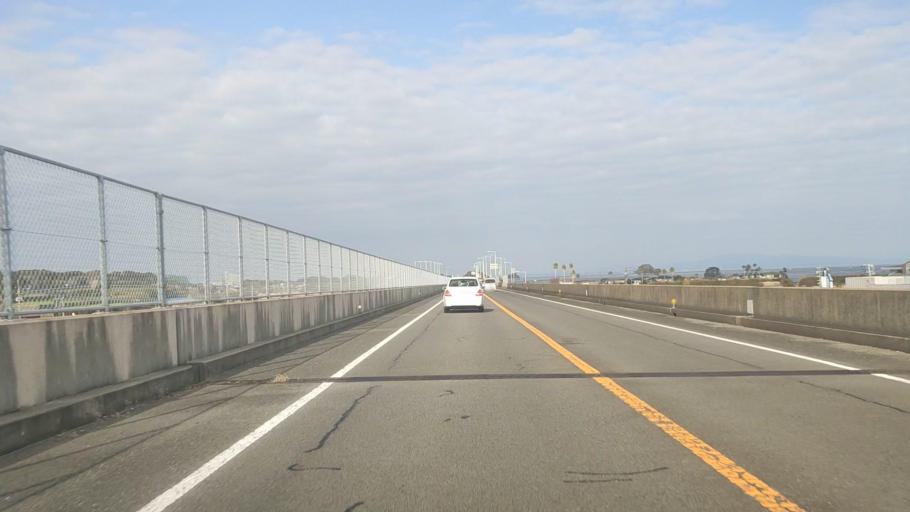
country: JP
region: Nagasaki
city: Shimabara
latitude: 32.7432
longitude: 130.3721
